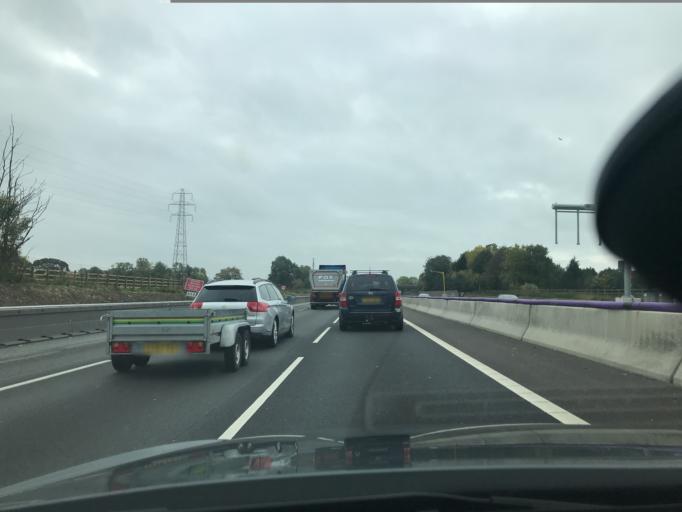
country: GB
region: England
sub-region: Cheshire East
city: Knutsford
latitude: 53.2728
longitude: -2.3987
